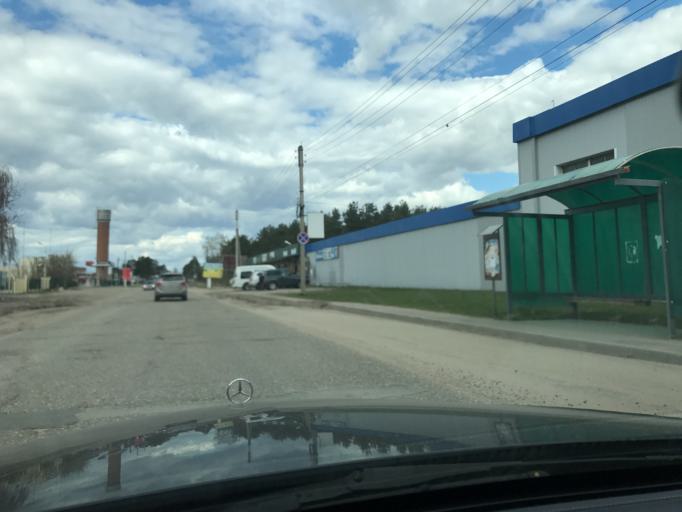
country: RU
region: Vladimir
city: Pokrov
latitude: 55.9007
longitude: 39.1978
